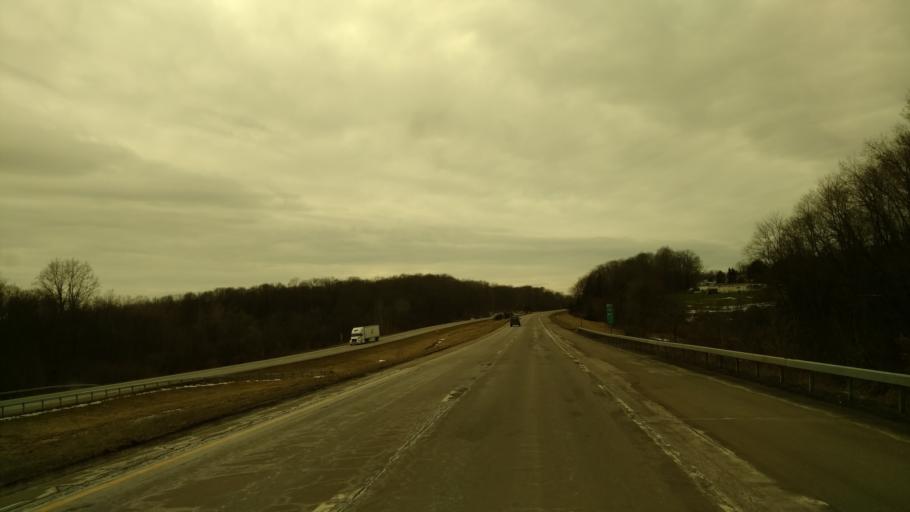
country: US
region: New York
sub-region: Chautauqua County
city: Lakewood
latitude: 42.1284
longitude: -79.3116
